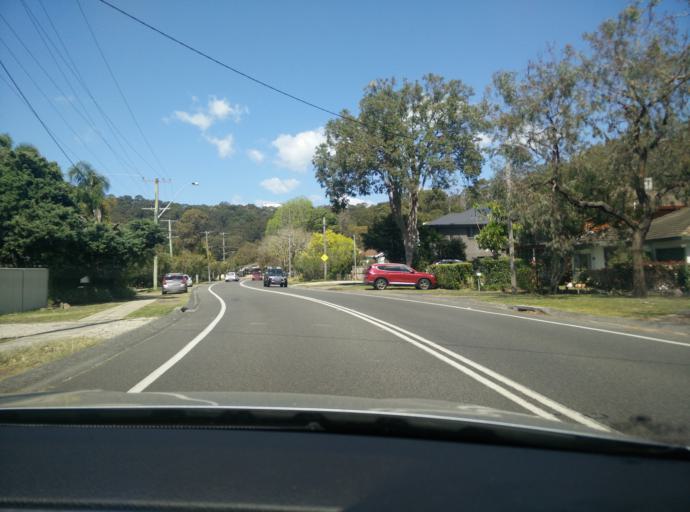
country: AU
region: New South Wales
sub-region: Gosford Shire
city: Umina
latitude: -33.5302
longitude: 151.3069
